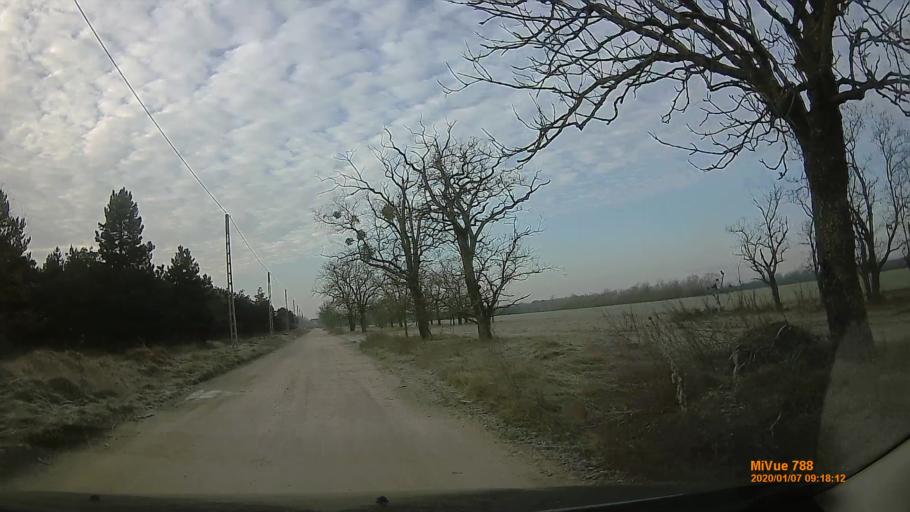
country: HU
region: Gyor-Moson-Sopron
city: Rajka
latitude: 47.9608
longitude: 17.1678
